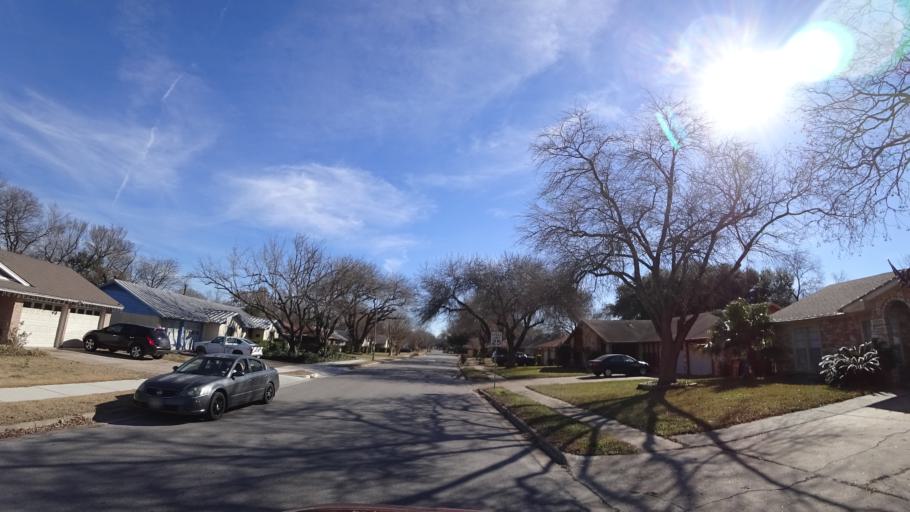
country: US
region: Texas
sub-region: Travis County
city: Wells Branch
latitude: 30.3781
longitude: -97.7074
